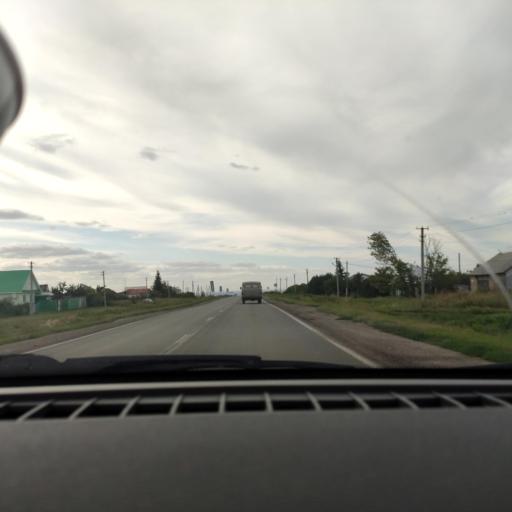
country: RU
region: Samara
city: Krasnyy Yar
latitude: 53.4444
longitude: 50.5284
